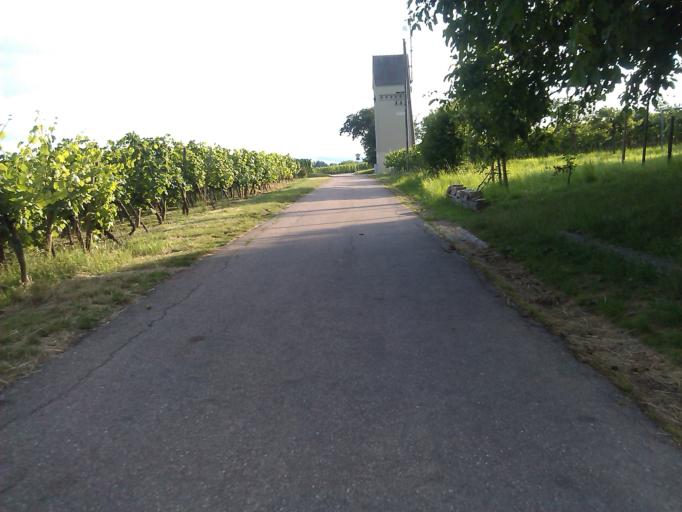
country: DE
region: Baden-Wuerttemberg
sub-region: Regierungsbezirk Stuttgart
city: Kirchheim am Neckar
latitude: 49.0507
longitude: 9.1487
